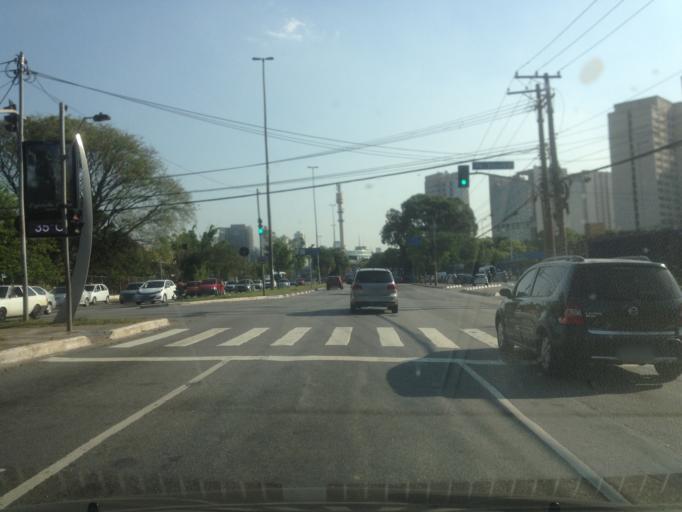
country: BR
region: Sao Paulo
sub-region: Sao Paulo
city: Sao Paulo
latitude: -23.5203
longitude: -46.6574
